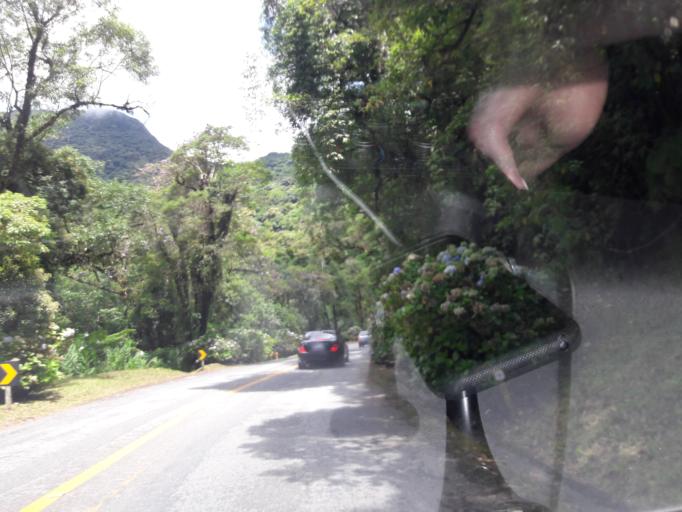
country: BR
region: Parana
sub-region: Campina Grande Do Sul
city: Campina Grande do Sul
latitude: -25.3323
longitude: -48.8970
